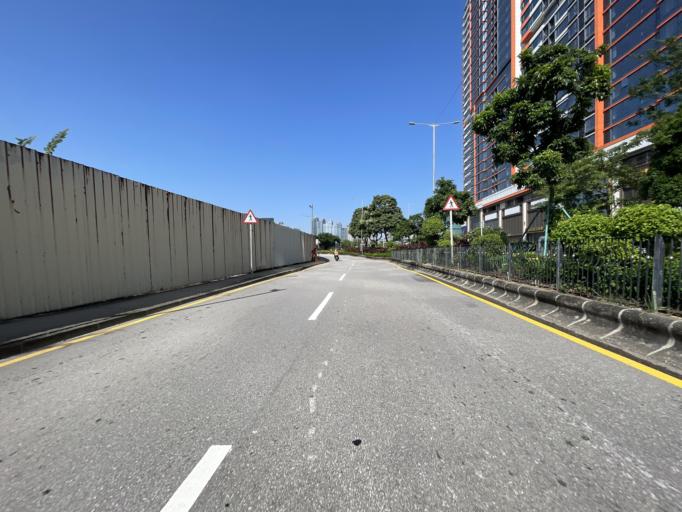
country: MO
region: Macau
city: Macau
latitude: 22.1304
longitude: 113.5586
